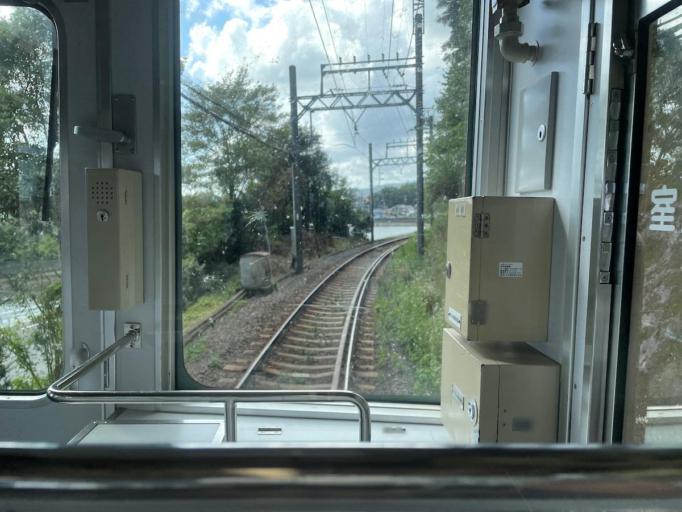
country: JP
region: Mie
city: Toba
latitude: 34.4605
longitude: 136.8413
